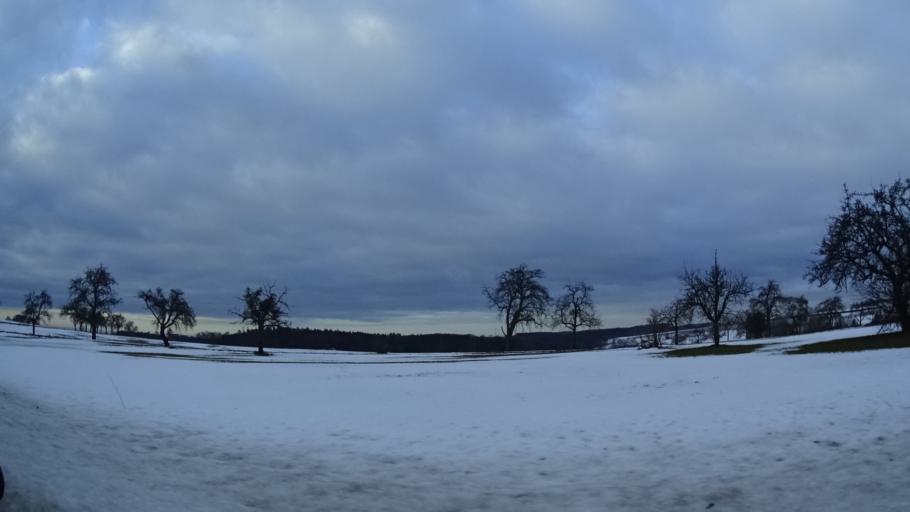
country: DE
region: Baden-Wuerttemberg
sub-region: Karlsruhe Region
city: Fahrenbach
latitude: 49.4622
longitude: 9.0940
